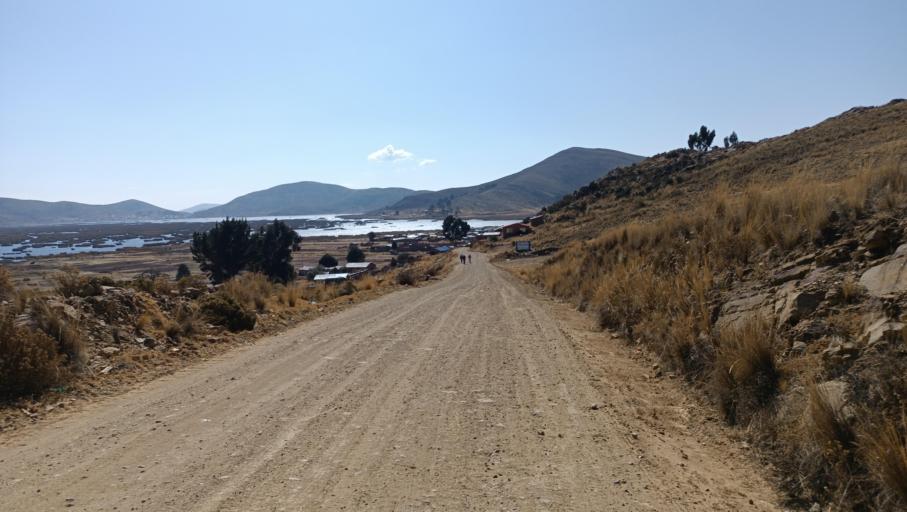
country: BO
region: La Paz
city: Batallas
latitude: -16.3482
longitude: -68.6728
